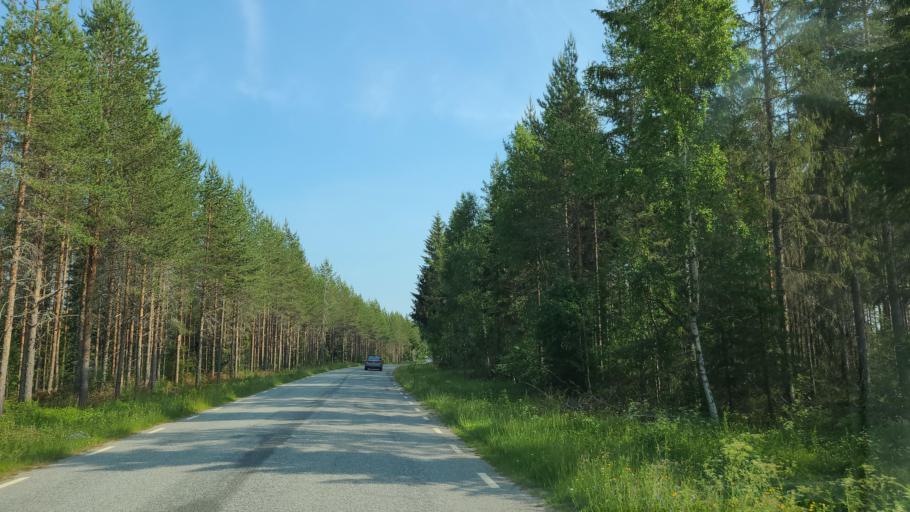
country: SE
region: Vaesterbotten
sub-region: Skelleftea Kommun
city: Burea
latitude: 64.3619
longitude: 21.3330
